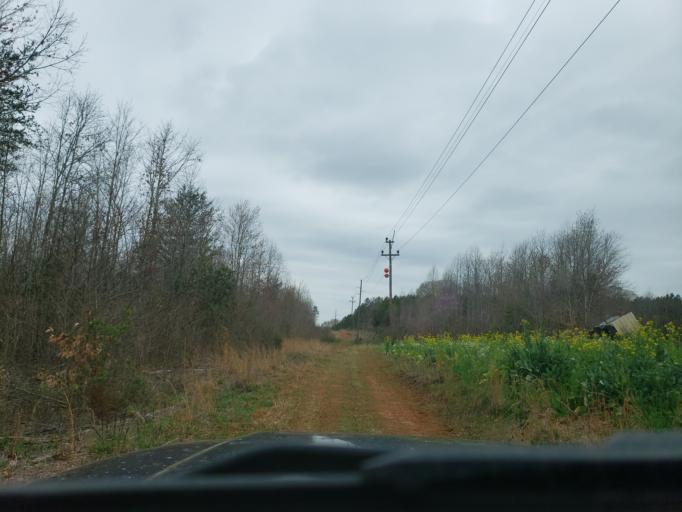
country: US
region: North Carolina
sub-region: Cleveland County
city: White Plains
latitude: 35.1876
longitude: -81.3704
